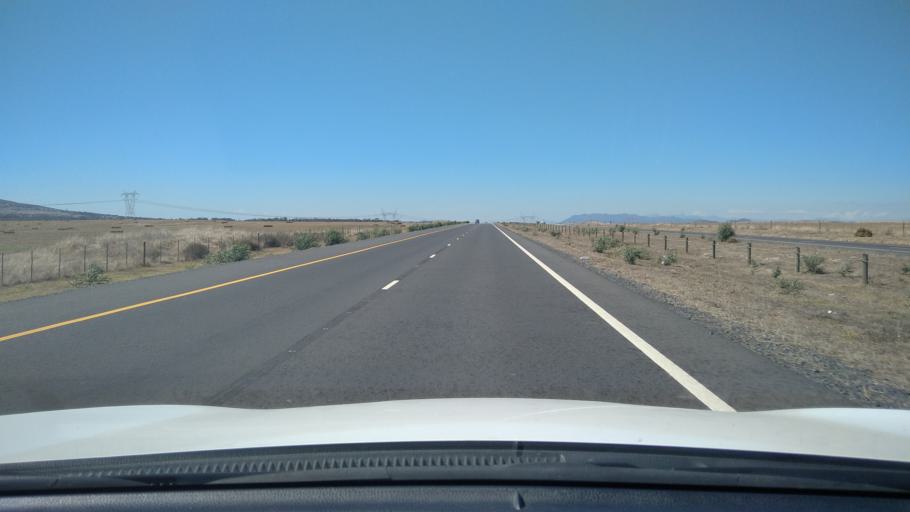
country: ZA
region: Western Cape
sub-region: City of Cape Town
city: Atlantis
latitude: -33.6349
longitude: 18.5780
